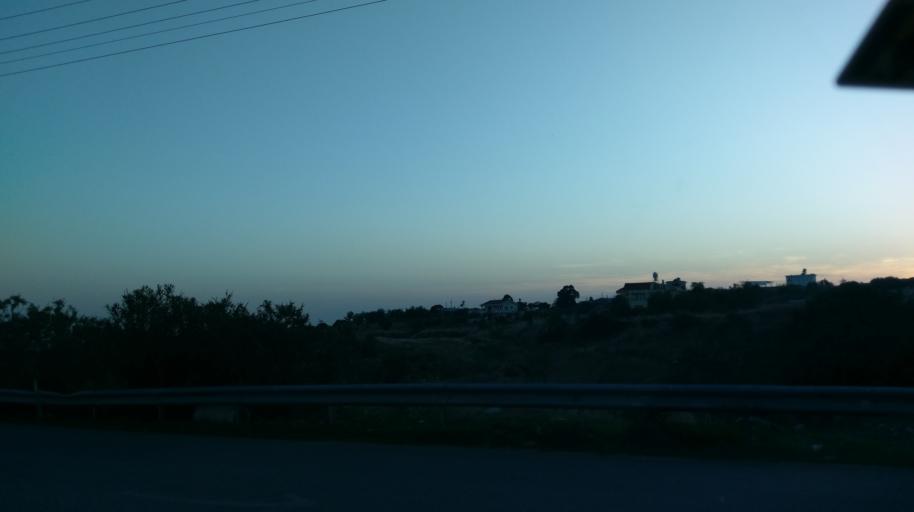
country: CY
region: Ammochostos
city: Trikomo
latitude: 35.3382
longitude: 33.8739
